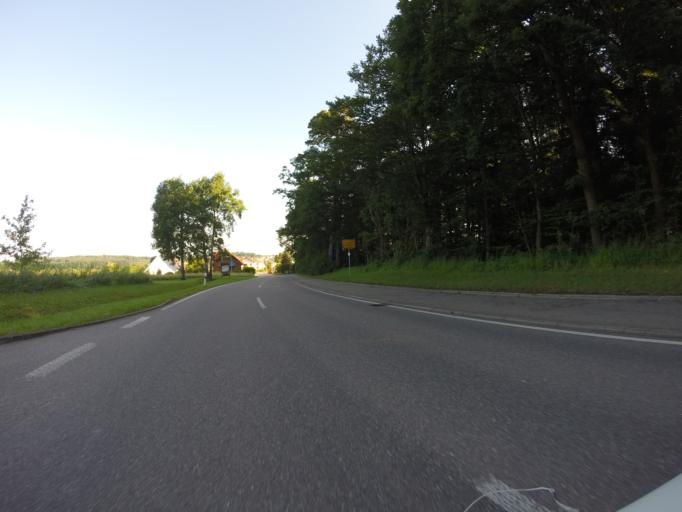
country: DE
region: Baden-Wuerttemberg
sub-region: Karlsruhe Region
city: Dobel
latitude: 48.8496
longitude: 8.5130
